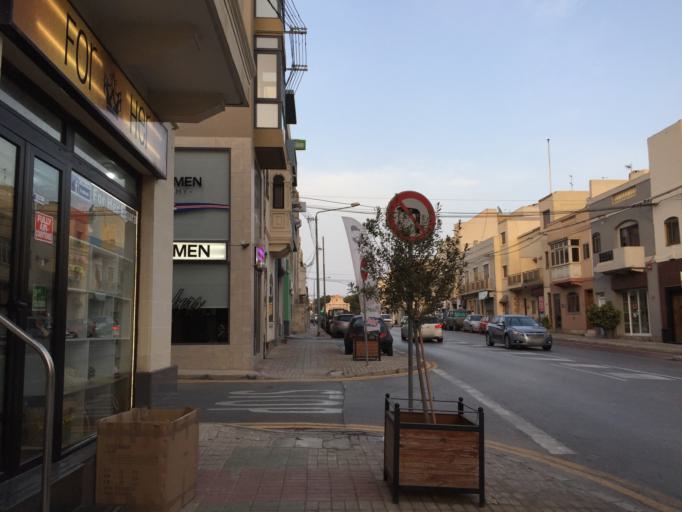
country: MT
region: Il-Fgura
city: Fgura
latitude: 35.8724
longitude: 14.5242
